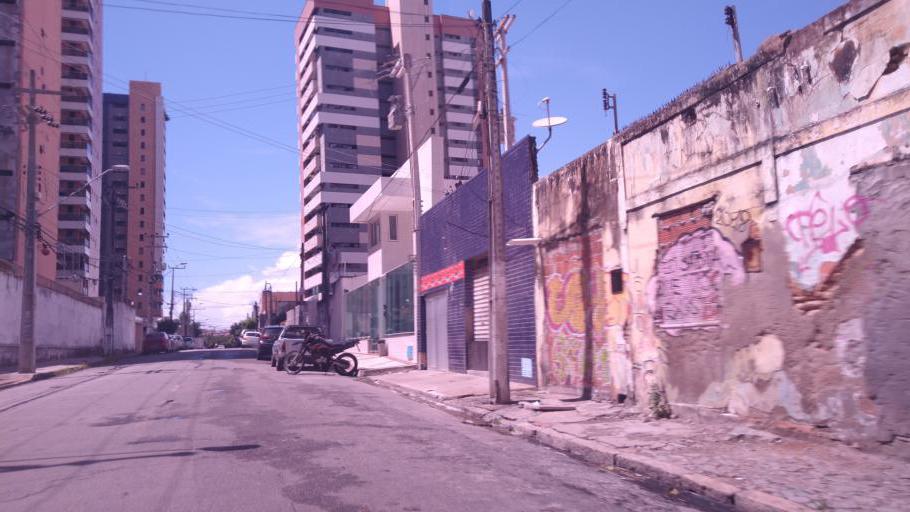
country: BR
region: Ceara
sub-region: Fortaleza
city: Fortaleza
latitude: -3.7250
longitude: -38.4865
